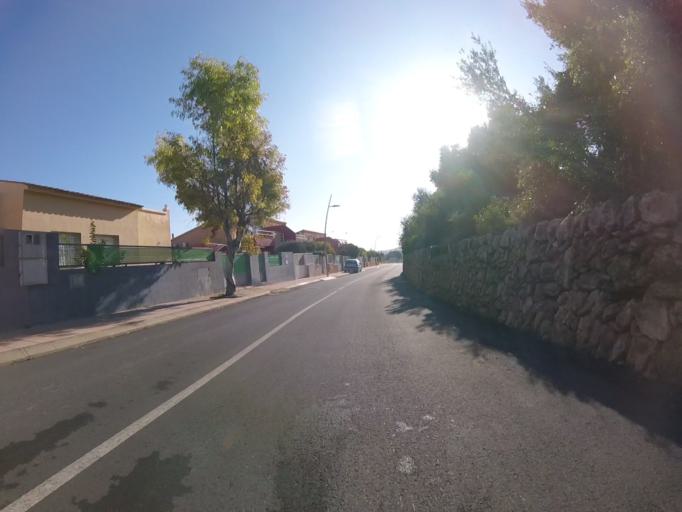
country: ES
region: Valencia
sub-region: Provincia de Castello
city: Peniscola
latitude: 40.3882
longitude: 0.3766
